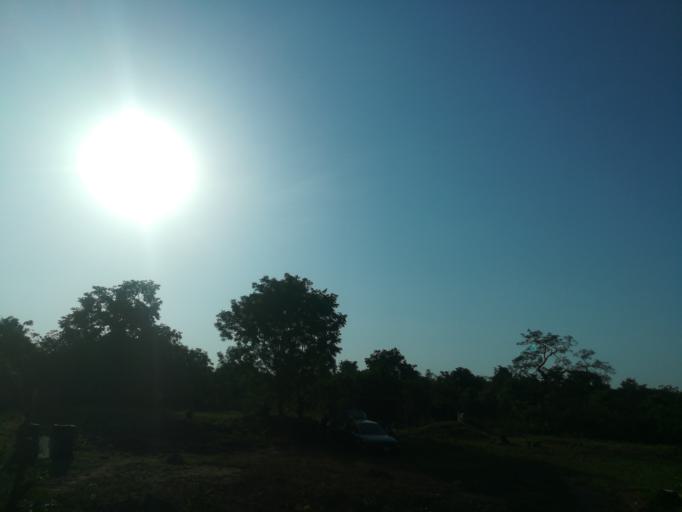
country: NG
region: Ogun
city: Abeokuta
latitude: 7.2471
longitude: 3.3005
